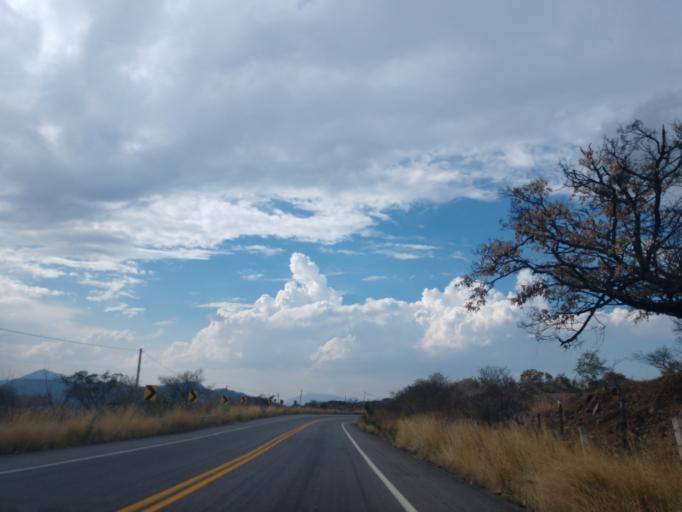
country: MX
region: Jalisco
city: La Manzanilla de la Paz
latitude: 20.1090
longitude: -103.1647
